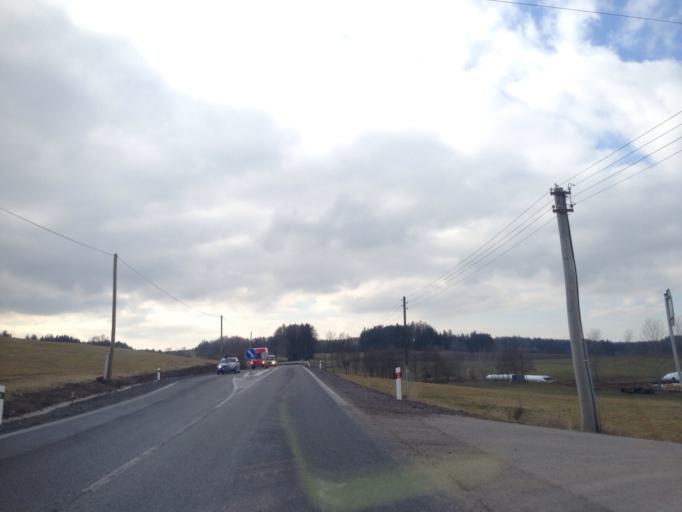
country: CZ
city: Horni Branna
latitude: 50.5869
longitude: 15.5859
